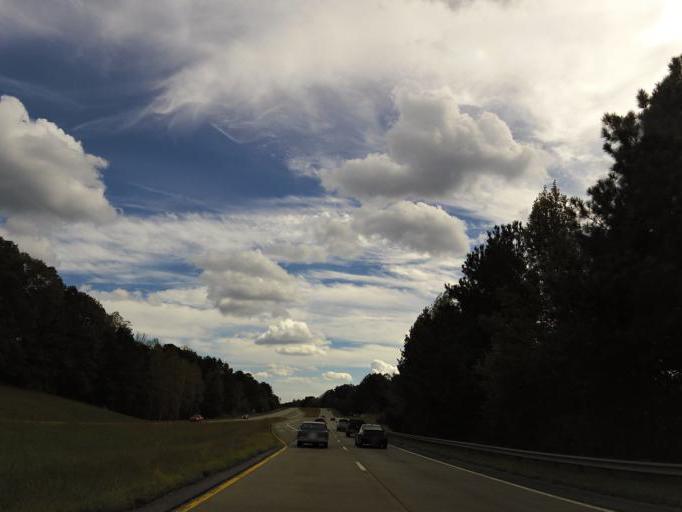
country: US
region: Georgia
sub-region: Pickens County
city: Jasper
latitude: 34.4168
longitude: -84.4287
